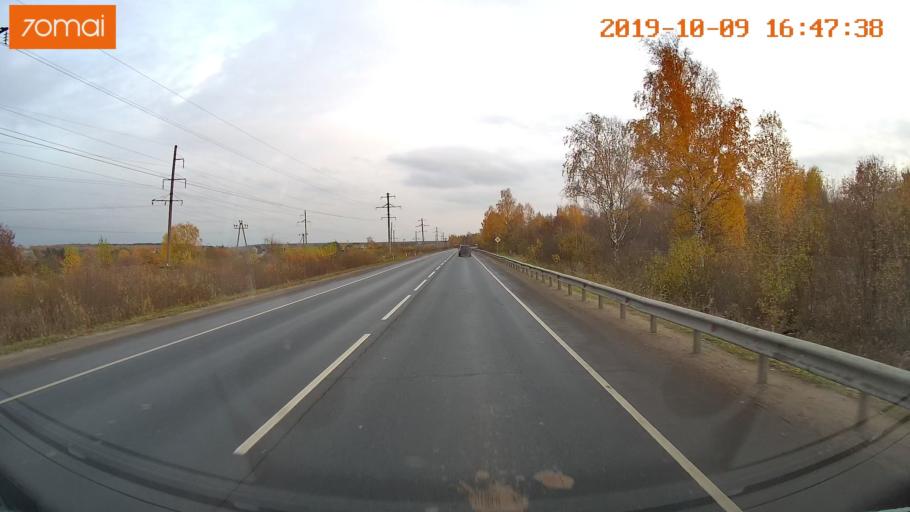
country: RU
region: Kostroma
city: Volgorechensk
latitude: 57.4355
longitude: 41.1807
